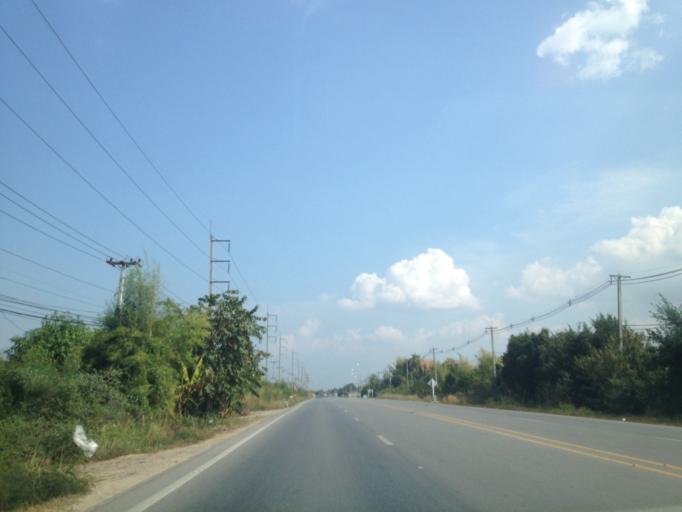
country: TH
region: Chiang Mai
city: Chom Thong
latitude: 18.3313
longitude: 98.6703
